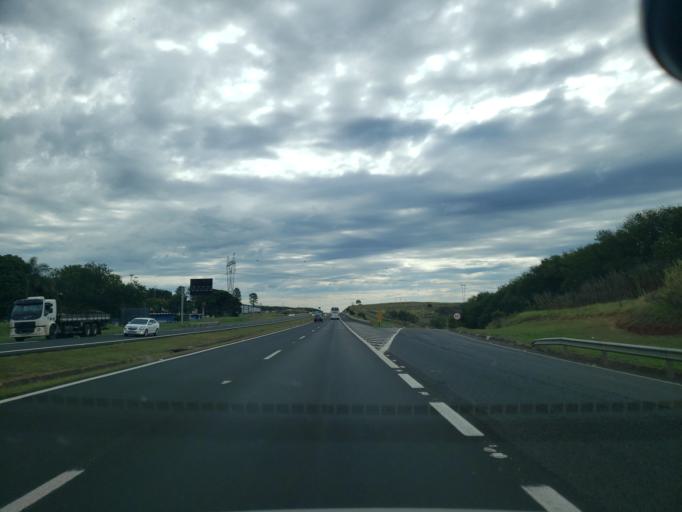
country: BR
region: Sao Paulo
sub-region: Bauru
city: Bauru
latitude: -22.2766
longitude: -49.0925
